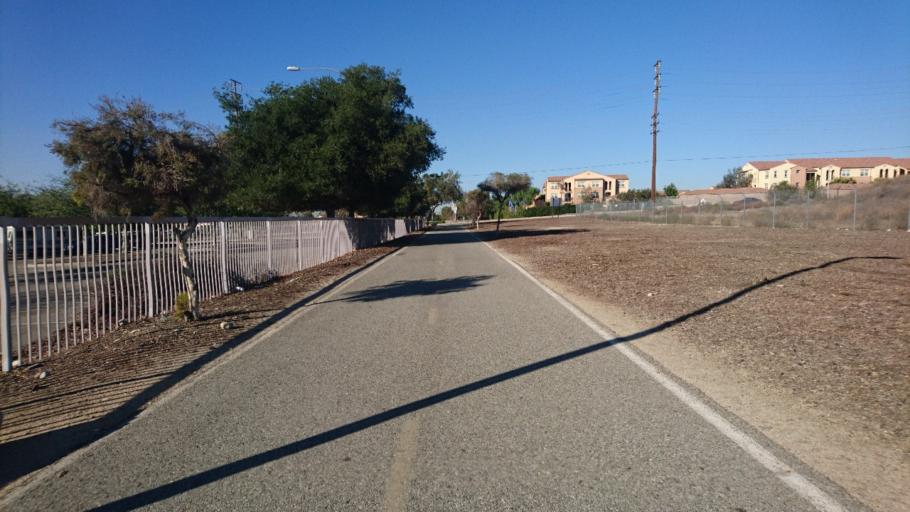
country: US
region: California
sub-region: San Bernardino County
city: Montclair
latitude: 34.0959
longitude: -117.6972
